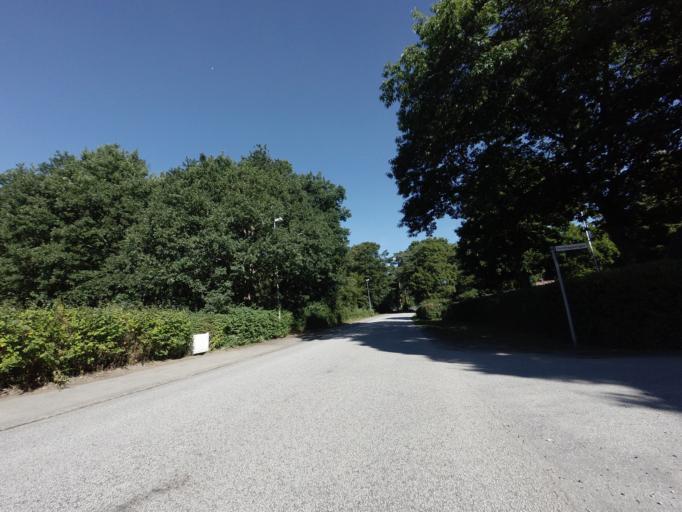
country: SE
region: Skane
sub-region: Ystads Kommun
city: Ystad
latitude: 55.4289
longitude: 13.8486
